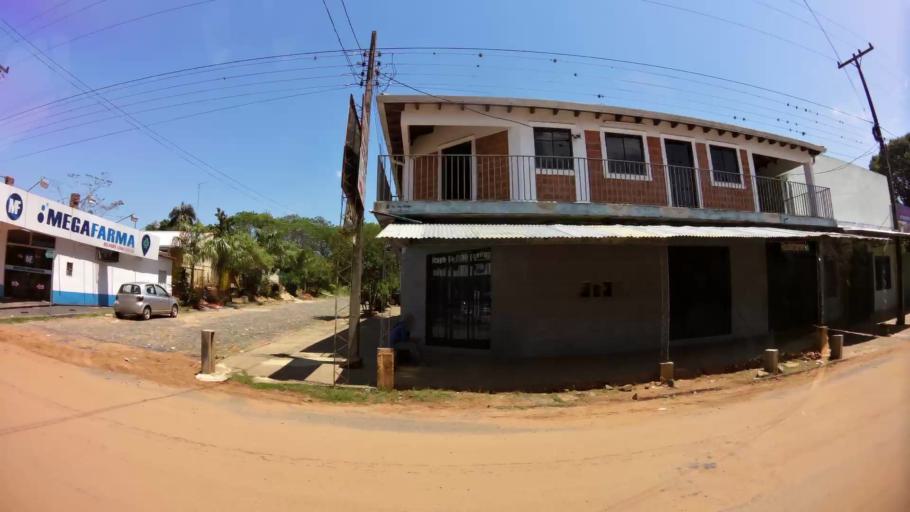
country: PY
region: Central
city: Nemby
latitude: -25.4079
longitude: -57.5259
